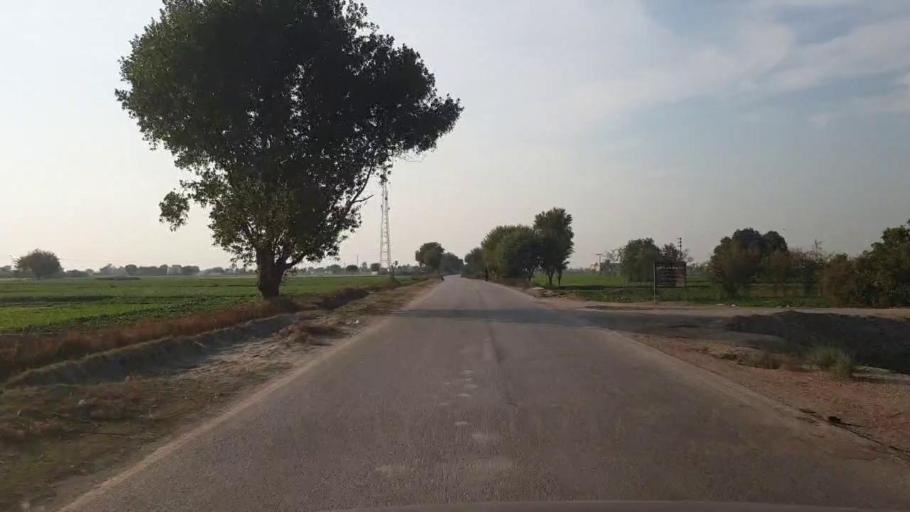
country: PK
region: Sindh
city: Shahpur Chakar
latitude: 26.1599
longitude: 68.6370
